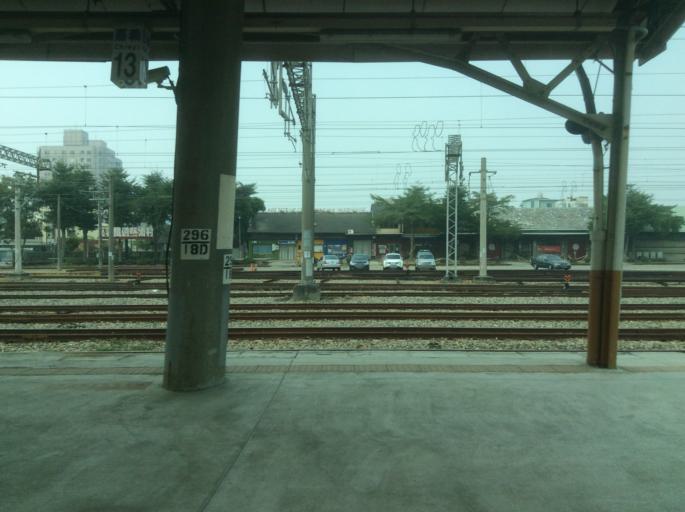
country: TW
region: Taiwan
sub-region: Chiayi
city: Jiayi Shi
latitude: 23.4807
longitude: 120.4420
